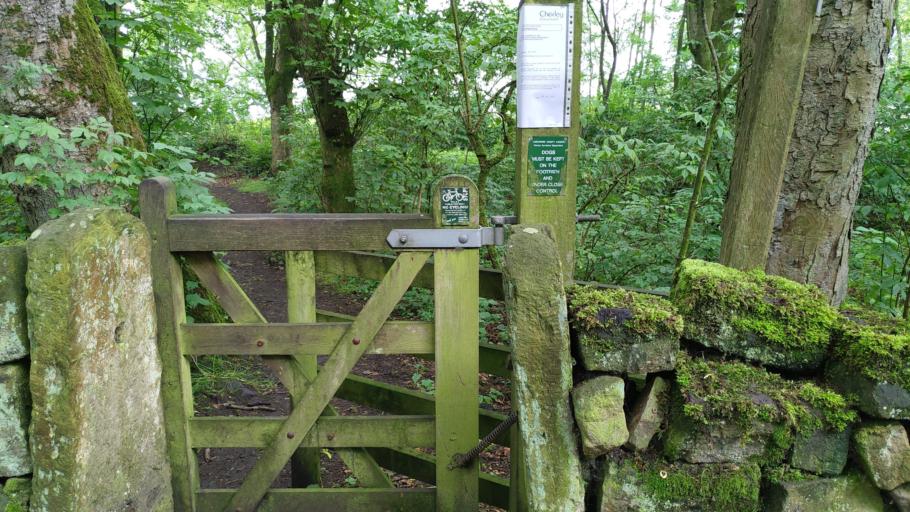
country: GB
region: England
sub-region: Lancashire
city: Chorley
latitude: 53.6807
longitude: -2.5722
